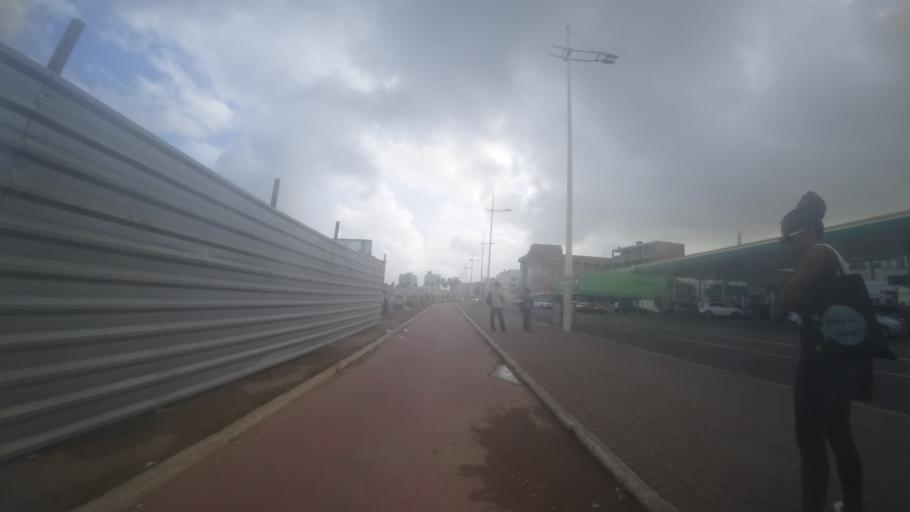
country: BR
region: Bahia
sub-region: Salvador
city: Salvador
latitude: -13.0104
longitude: -38.4650
